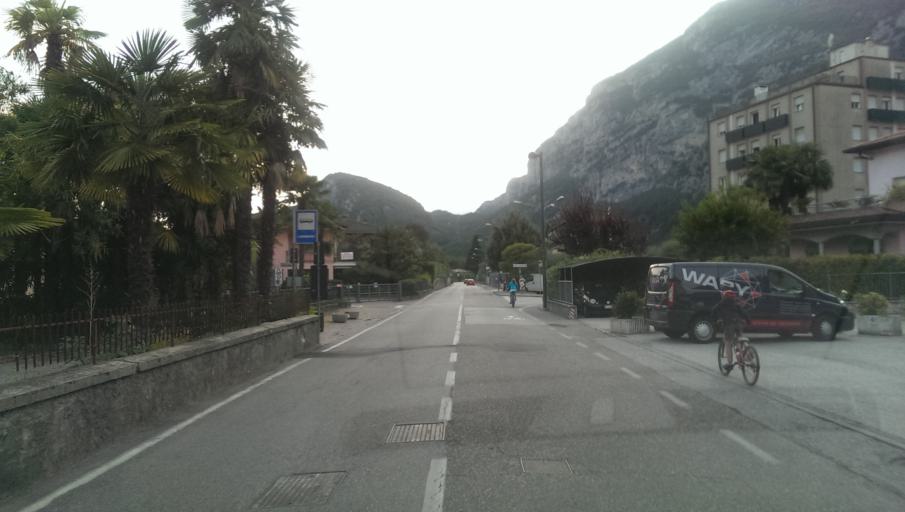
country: IT
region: Trentino-Alto Adige
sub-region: Provincia di Trento
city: Dro
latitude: 45.9588
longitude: 10.9069
